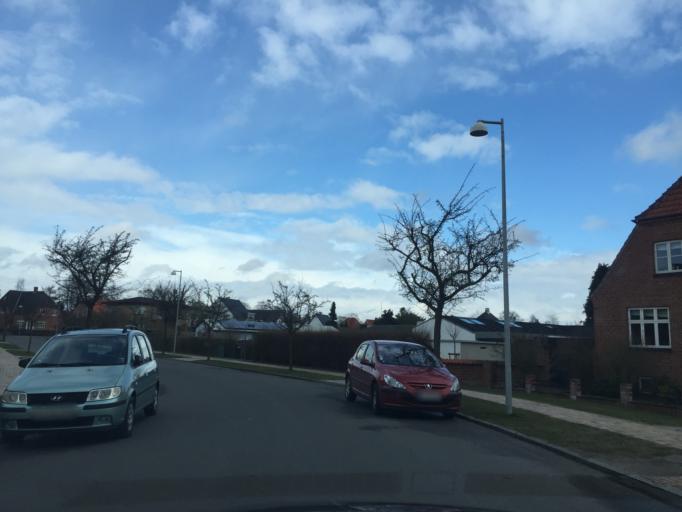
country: DK
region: South Denmark
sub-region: Odense Kommune
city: Odense
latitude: 55.3772
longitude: 10.3862
